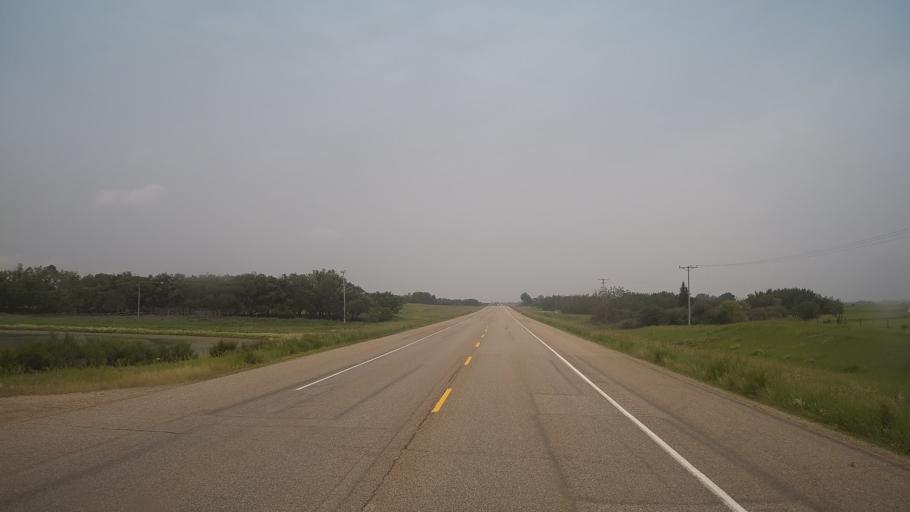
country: CA
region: Saskatchewan
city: Biggar
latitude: 52.0564
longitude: -107.9142
